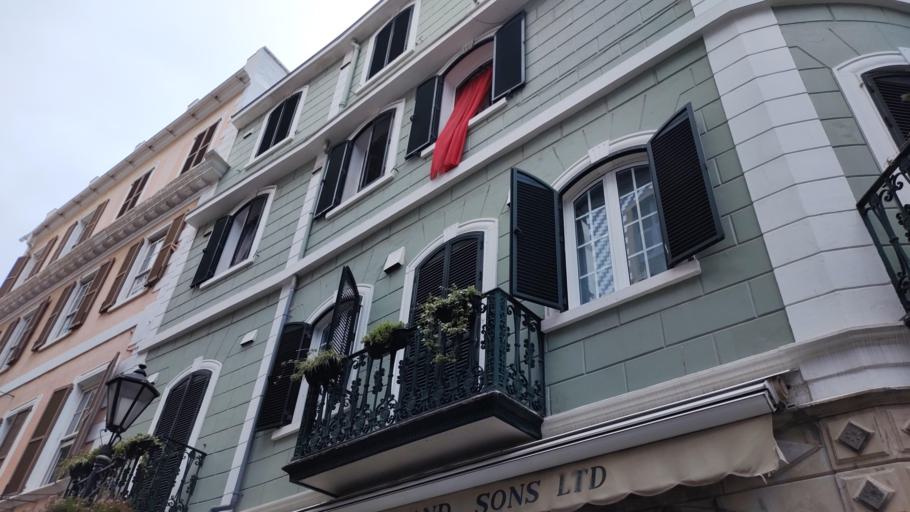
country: GI
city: Gibraltar
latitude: 36.1415
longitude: -5.3535
